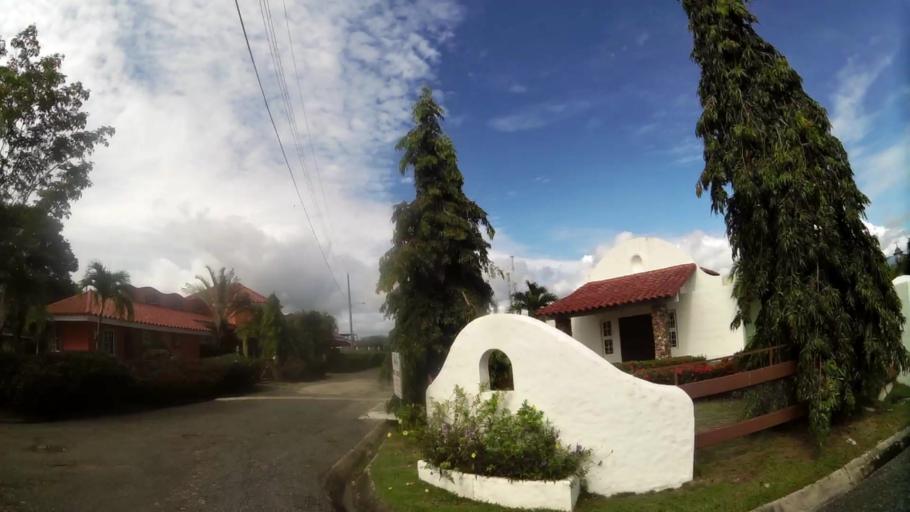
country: PA
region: Panama
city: Nueva Gorgona
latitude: 8.5448
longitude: -79.8821
